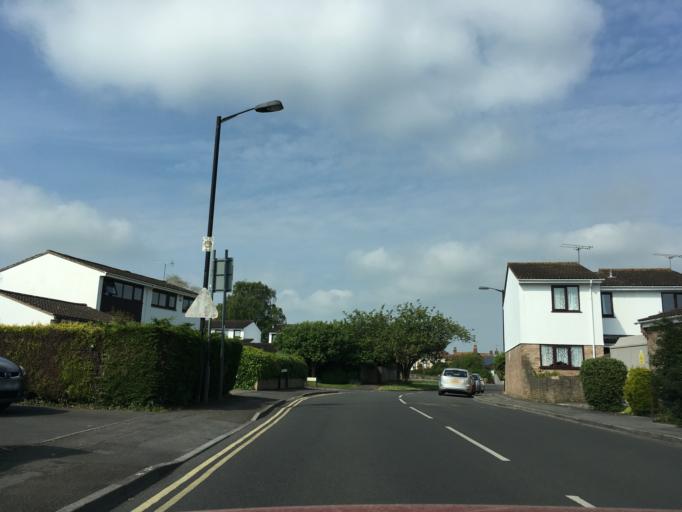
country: GB
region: England
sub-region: North Somerset
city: Nailsea
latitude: 51.4251
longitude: -2.7690
